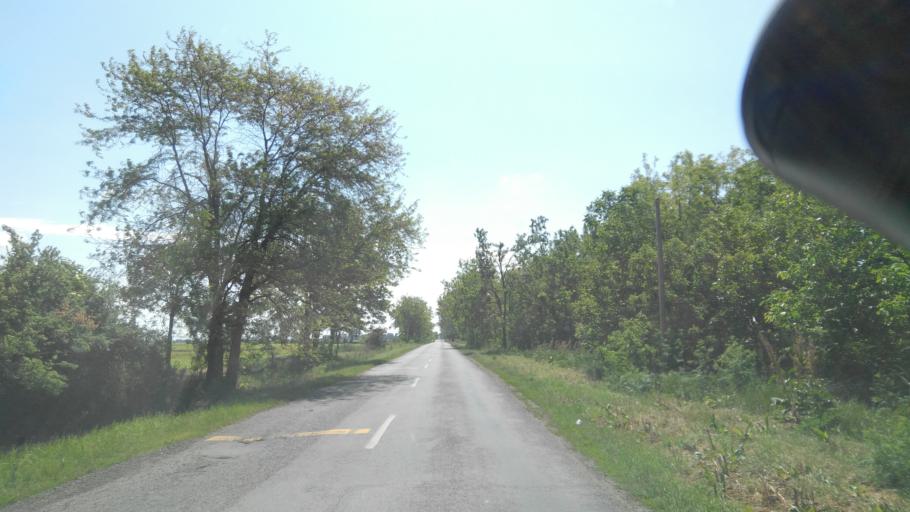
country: HU
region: Bekes
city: Magyarbanhegyes
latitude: 46.4425
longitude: 20.9875
